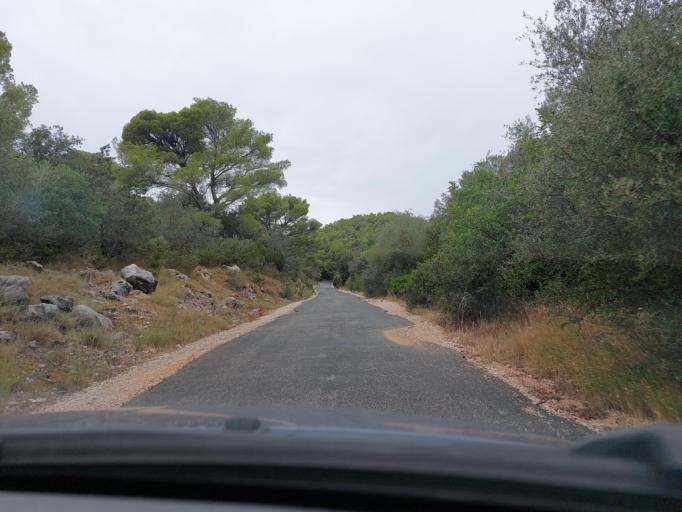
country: HR
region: Dubrovacko-Neretvanska
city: Smokvica
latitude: 42.7625
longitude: 16.9021
